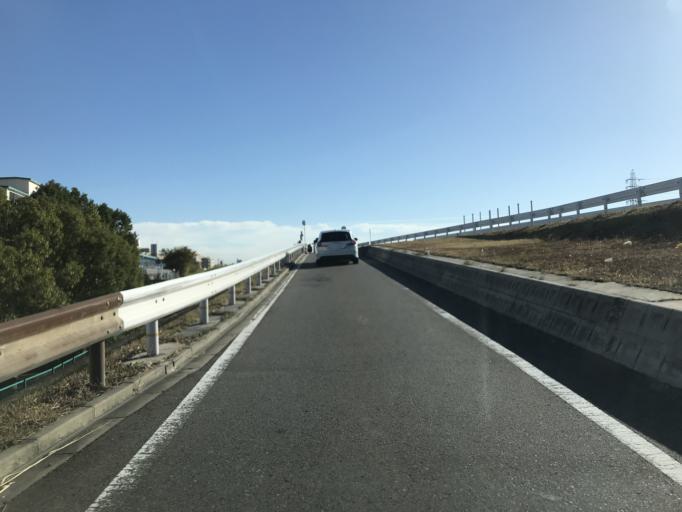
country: JP
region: Aichi
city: Kanie
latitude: 35.1398
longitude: 136.8361
